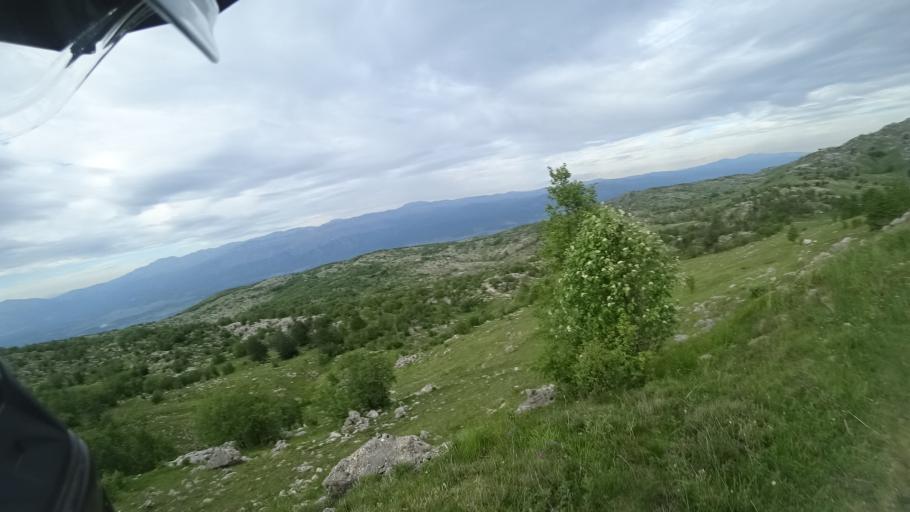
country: HR
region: Sibensko-Kniniska
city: Drnis
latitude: 43.8590
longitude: 16.3832
